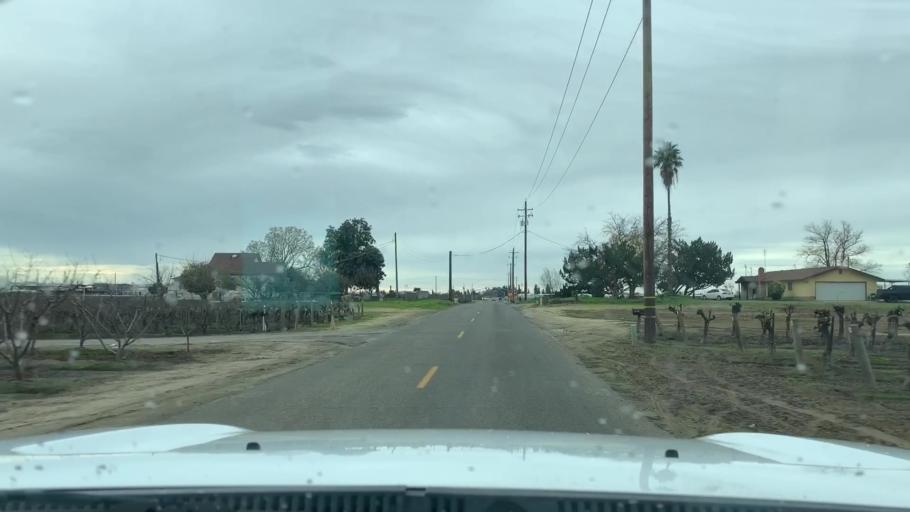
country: US
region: California
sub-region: Fresno County
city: Selma
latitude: 36.5507
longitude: -119.5751
